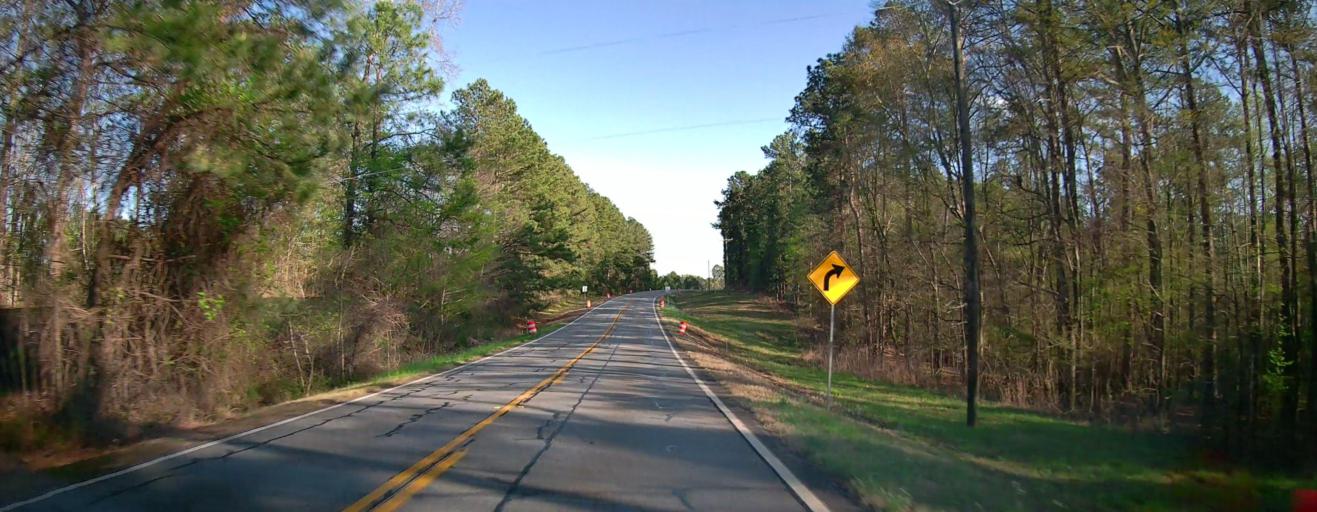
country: US
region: Georgia
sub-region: Baldwin County
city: Milledgeville
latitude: 33.1186
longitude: -83.2895
